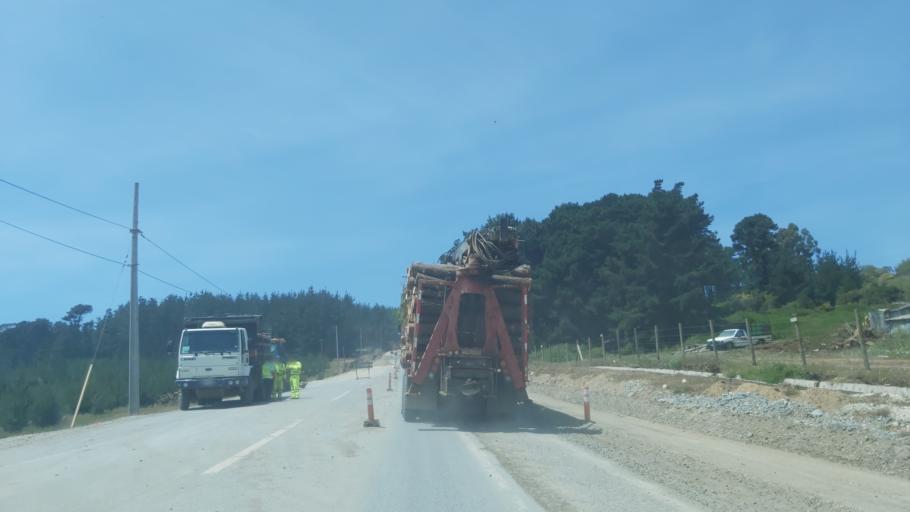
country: CL
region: Maule
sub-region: Provincia de Talca
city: Constitucion
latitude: -35.4505
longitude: -72.4786
